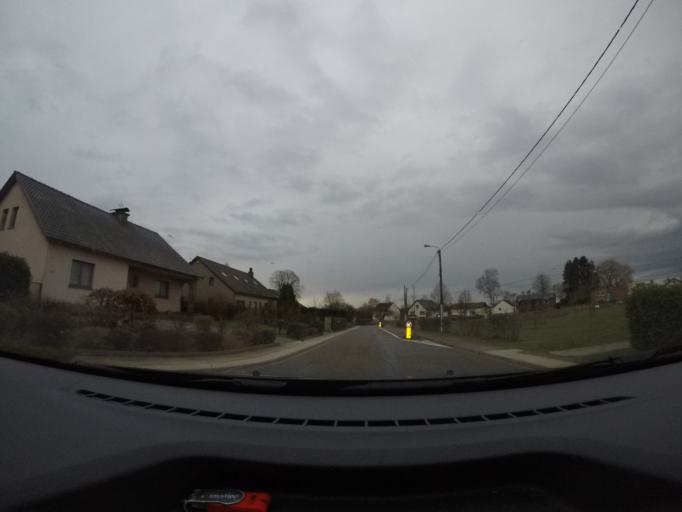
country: BE
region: Wallonia
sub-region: Province du Luxembourg
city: Tintigny
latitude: 49.6707
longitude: 5.4950
